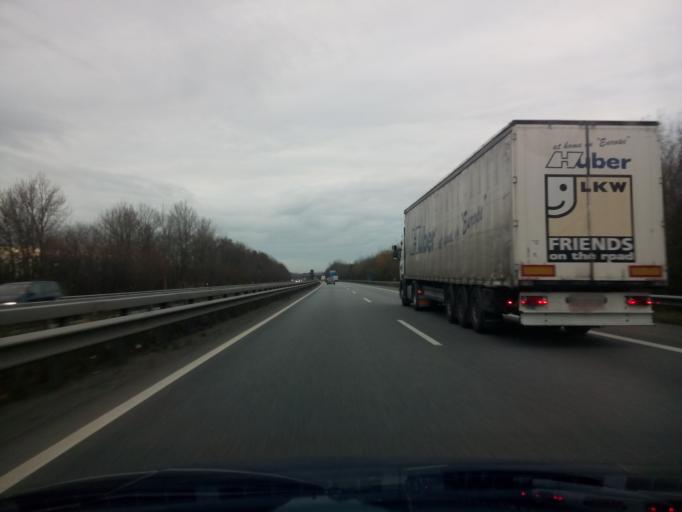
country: DE
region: Lower Saxony
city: Loxstedt
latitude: 53.4543
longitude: 8.5906
